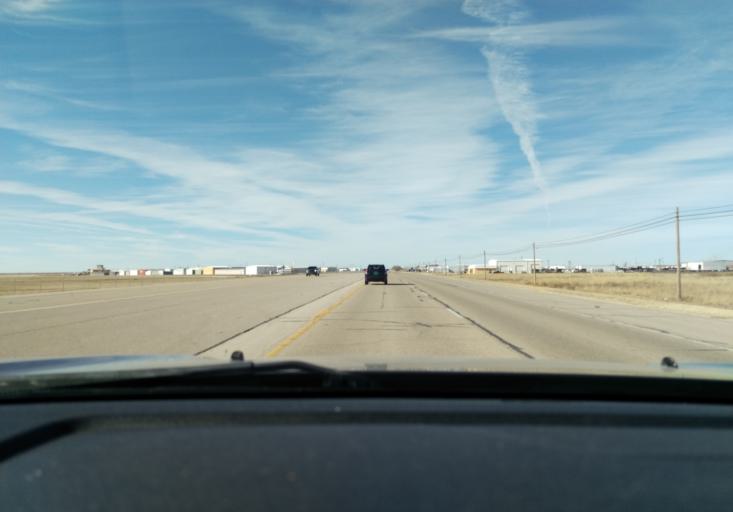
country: US
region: New Mexico
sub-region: Lea County
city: Hobbs
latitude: 32.6967
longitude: -103.2041
